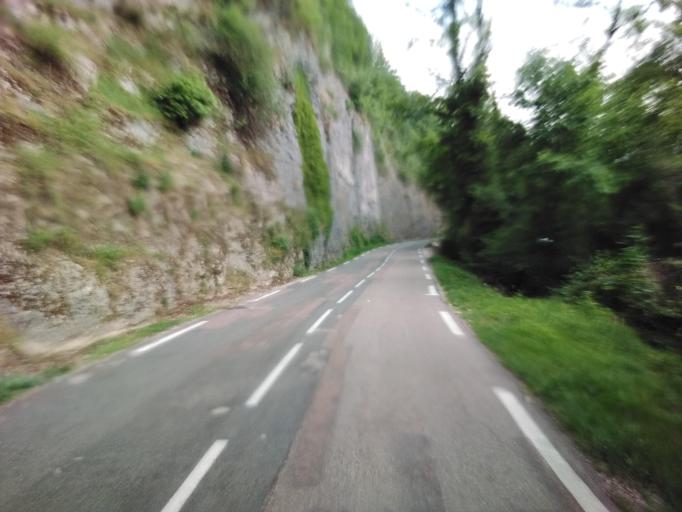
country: FR
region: Franche-Comte
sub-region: Departement du Jura
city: Arbois
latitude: 46.8721
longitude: 5.7988
